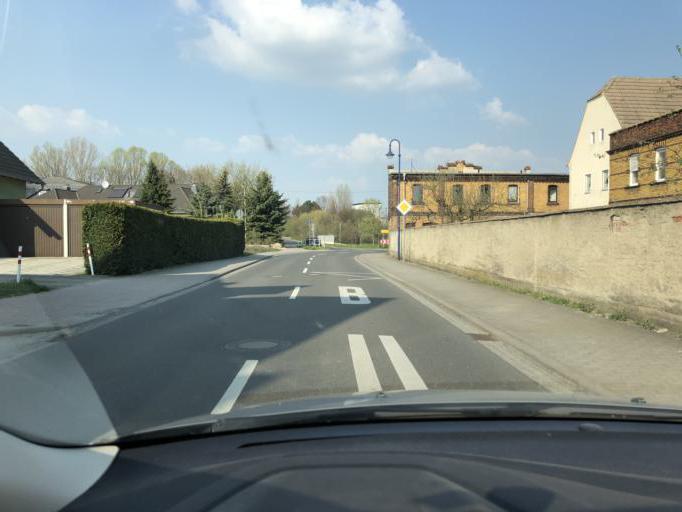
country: DE
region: Saxony
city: Rackwitz
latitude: 51.4349
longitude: 12.3746
